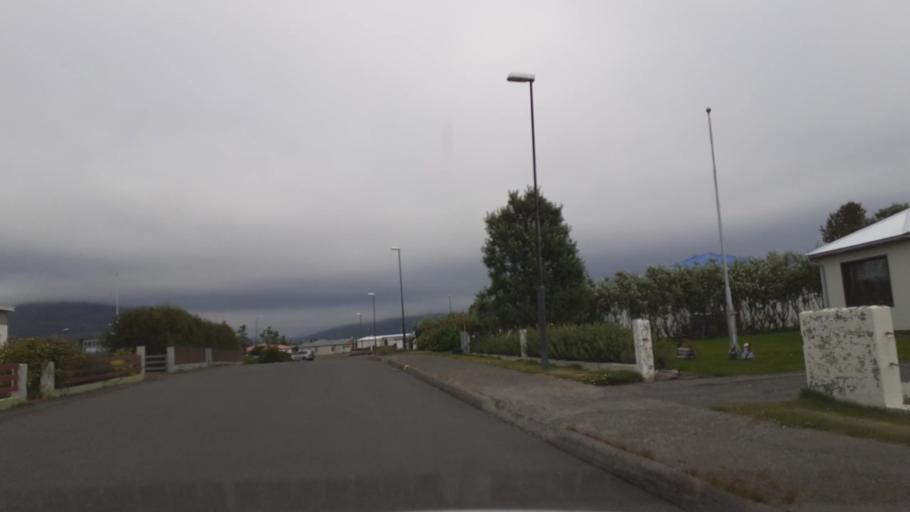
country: IS
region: Northwest
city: Saudarkrokur
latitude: 65.8984
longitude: -19.4140
